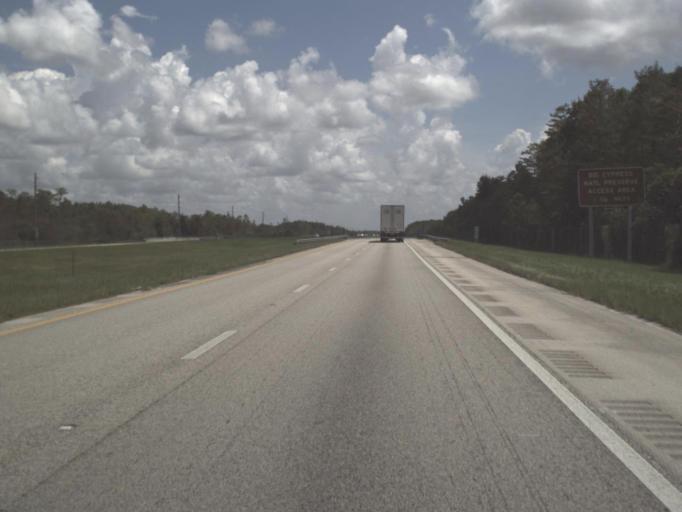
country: US
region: Florida
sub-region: Collier County
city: Immokalee
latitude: 26.1664
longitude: -81.2194
